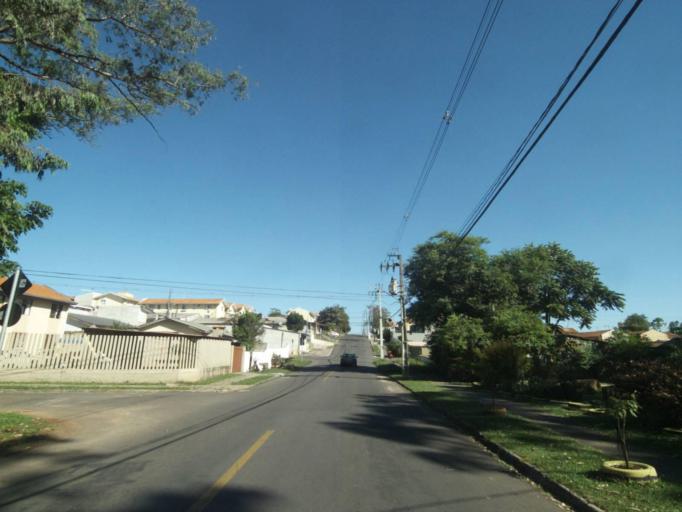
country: BR
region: Parana
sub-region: Curitiba
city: Curitiba
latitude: -25.4587
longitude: -49.3534
